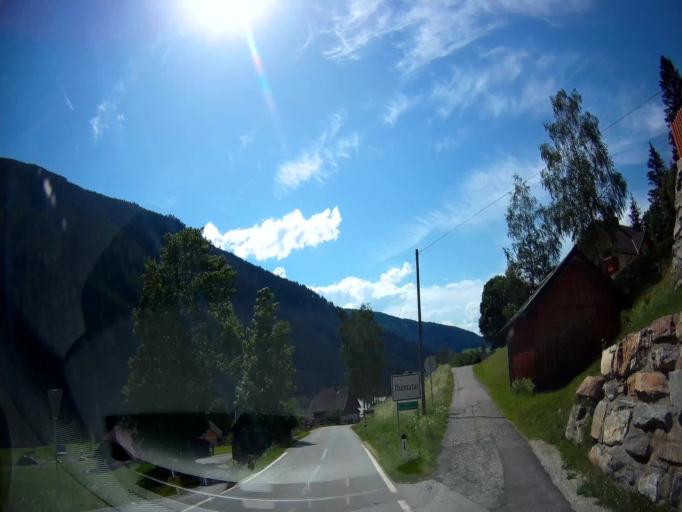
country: AT
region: Salzburg
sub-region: Politischer Bezirk Tamsweg
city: Thomatal
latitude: 47.0707
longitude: 13.7518
